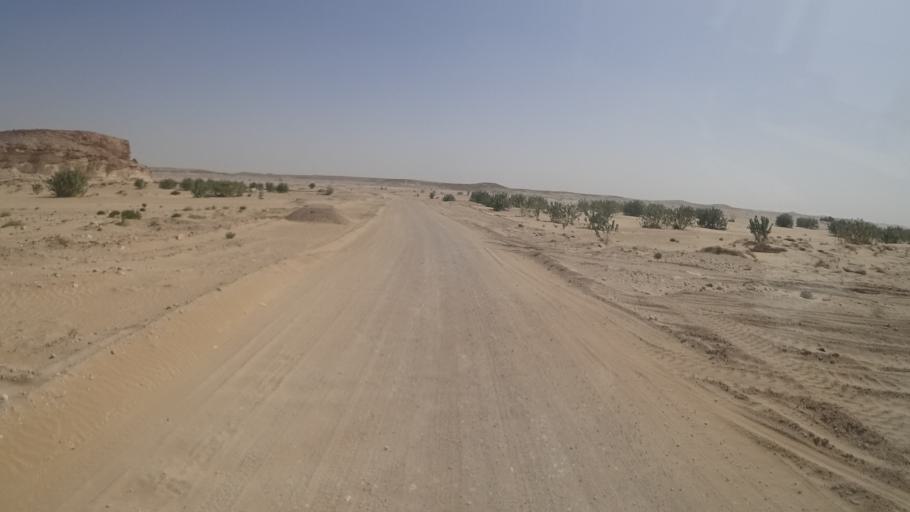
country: YE
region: Al Mahrah
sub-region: Shahan
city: Shihan as Sufla
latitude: 17.8780
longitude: 52.6047
